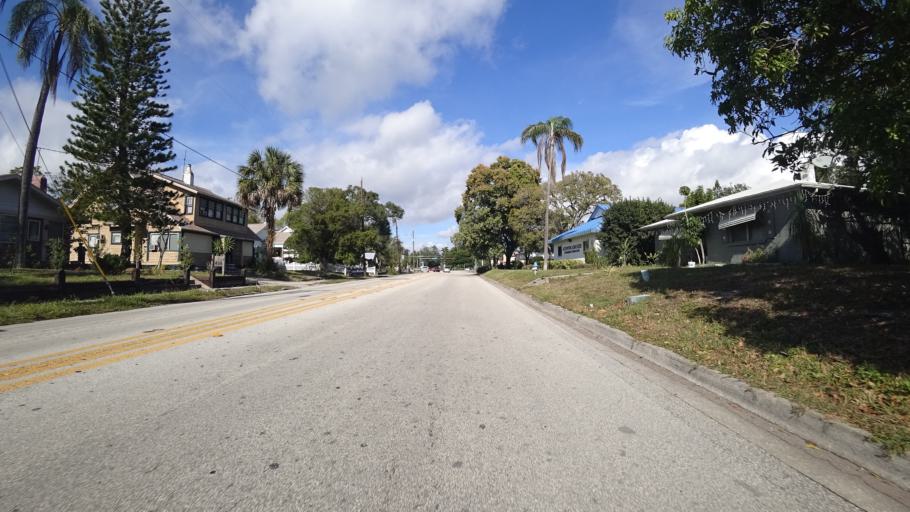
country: US
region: Florida
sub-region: Manatee County
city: Bradenton
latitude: 27.4939
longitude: -82.5875
